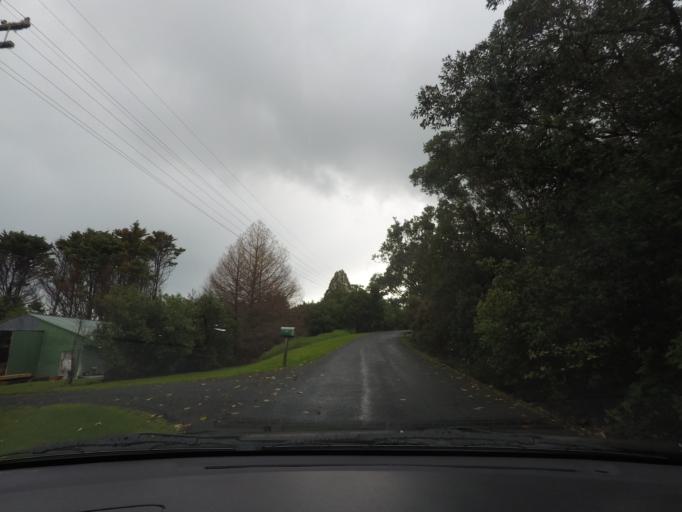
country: NZ
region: Auckland
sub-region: Auckland
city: Warkworth
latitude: -36.4729
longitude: 174.7359
